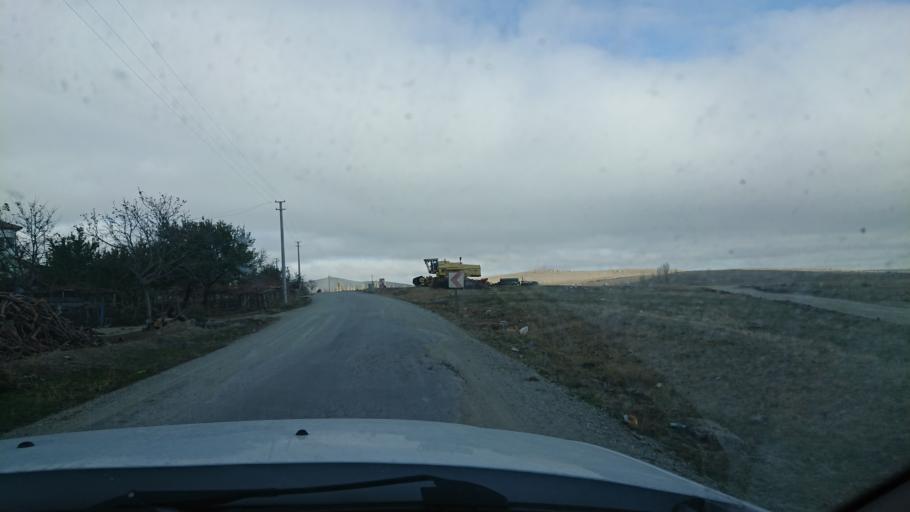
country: TR
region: Aksaray
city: Ortakoy
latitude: 38.7604
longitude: 34.0121
